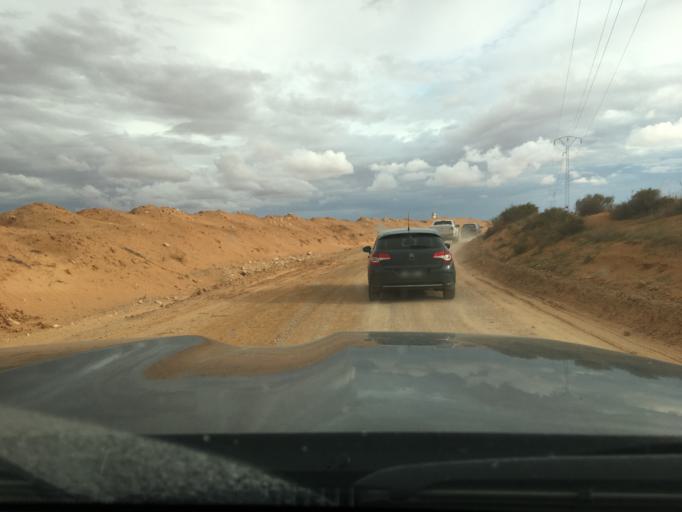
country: TN
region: Madanin
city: Medenine
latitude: 33.2727
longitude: 10.5656
